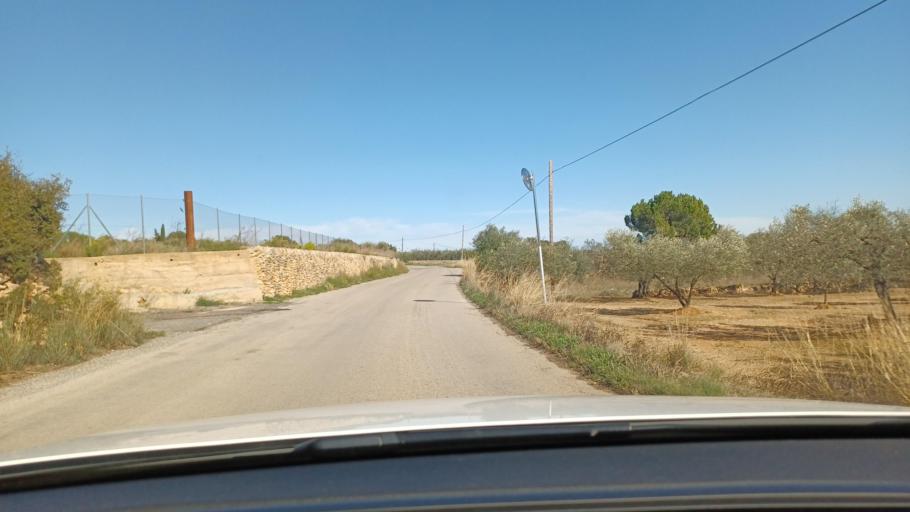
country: ES
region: Catalonia
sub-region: Provincia de Tarragona
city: Amposta
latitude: 40.6981
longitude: 0.5567
